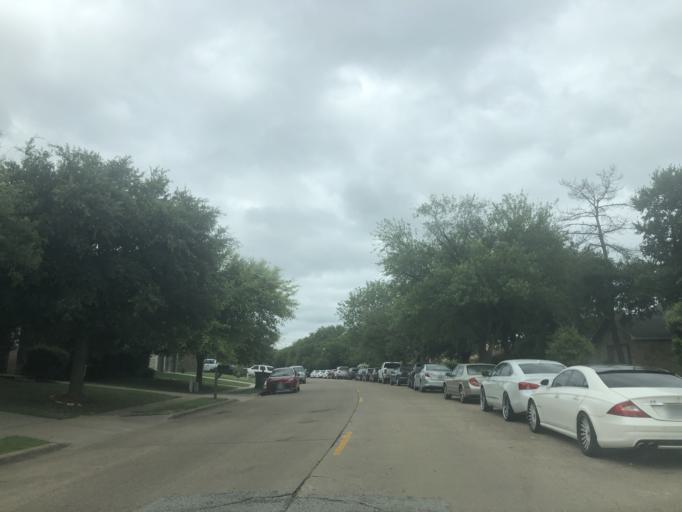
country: US
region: Texas
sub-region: Dallas County
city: Duncanville
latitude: 32.6360
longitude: -96.9437
